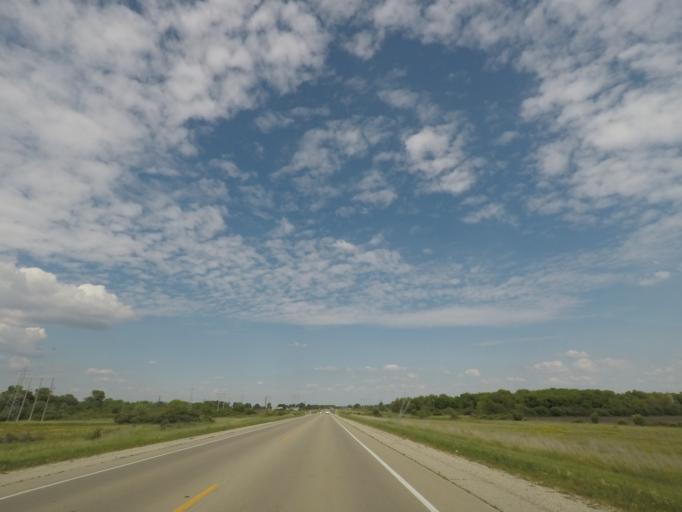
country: US
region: Wisconsin
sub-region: Walworth County
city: Whitewater
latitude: 42.8194
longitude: -88.7131
